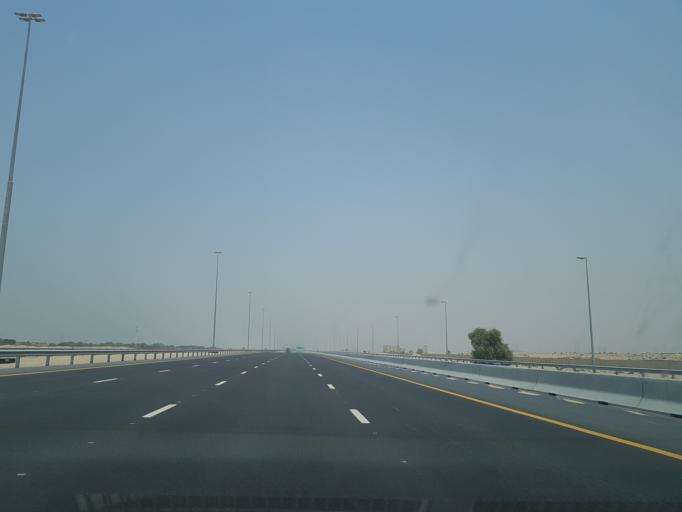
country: AE
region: Dubai
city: Dubai
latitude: 25.0453
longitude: 55.2786
